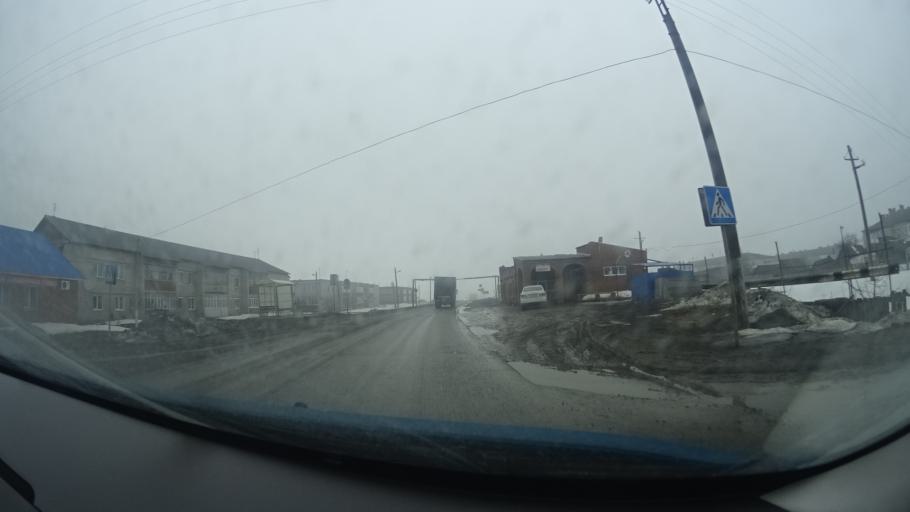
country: RU
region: Perm
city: Kuyeda
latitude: 56.4318
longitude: 55.5756
